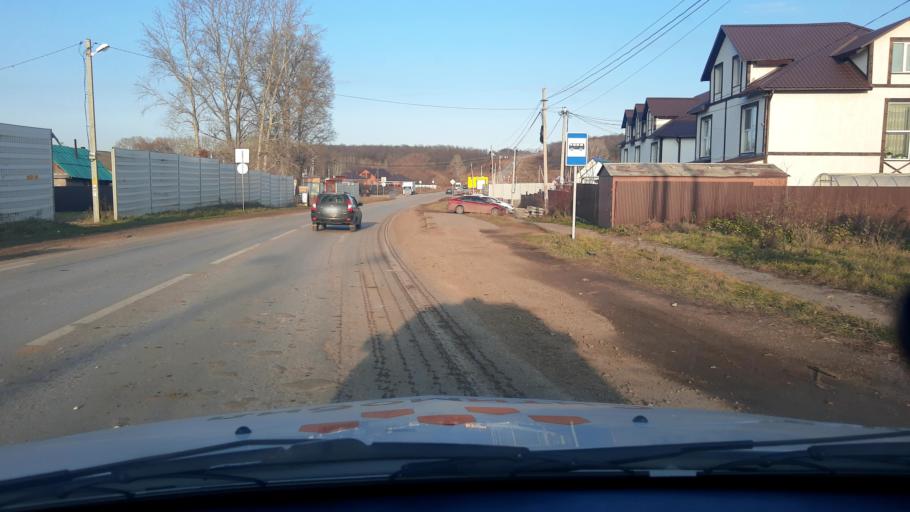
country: RU
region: Bashkortostan
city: Kabakovo
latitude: 54.6895
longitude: 56.1352
